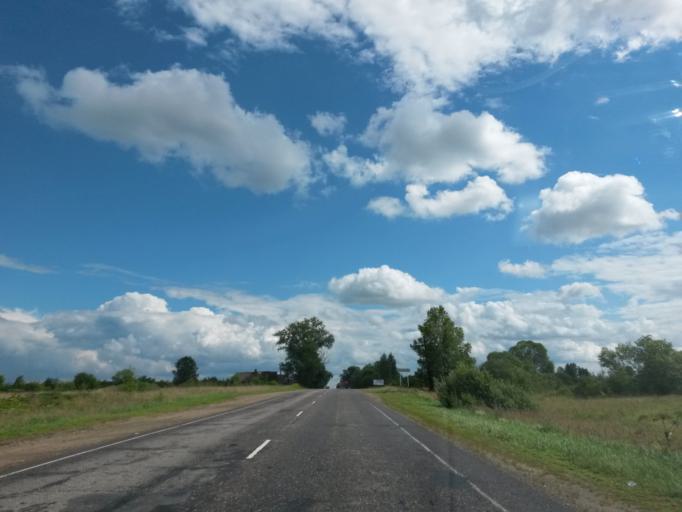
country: RU
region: Ivanovo
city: Pistsovo
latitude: 57.1913
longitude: 40.4157
